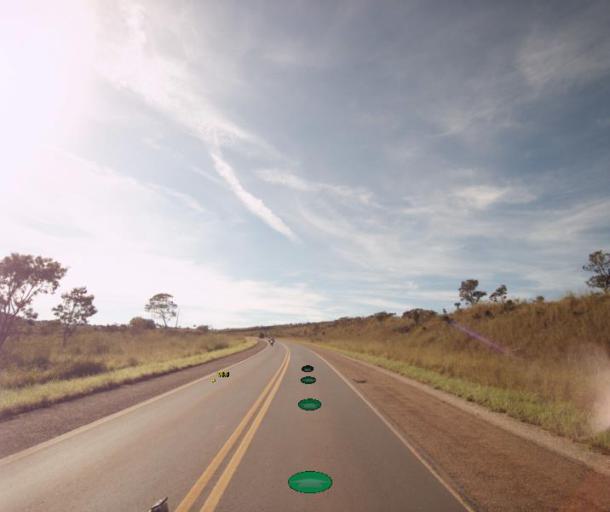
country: BR
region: Federal District
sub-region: Brasilia
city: Brasilia
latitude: -15.7536
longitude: -48.3466
